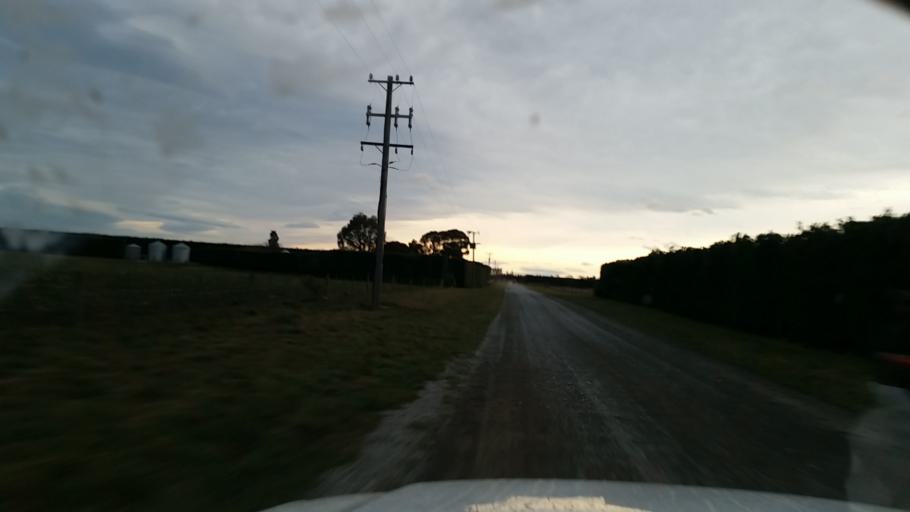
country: NZ
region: Canterbury
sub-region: Ashburton District
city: Tinwald
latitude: -43.8339
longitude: 171.6208
